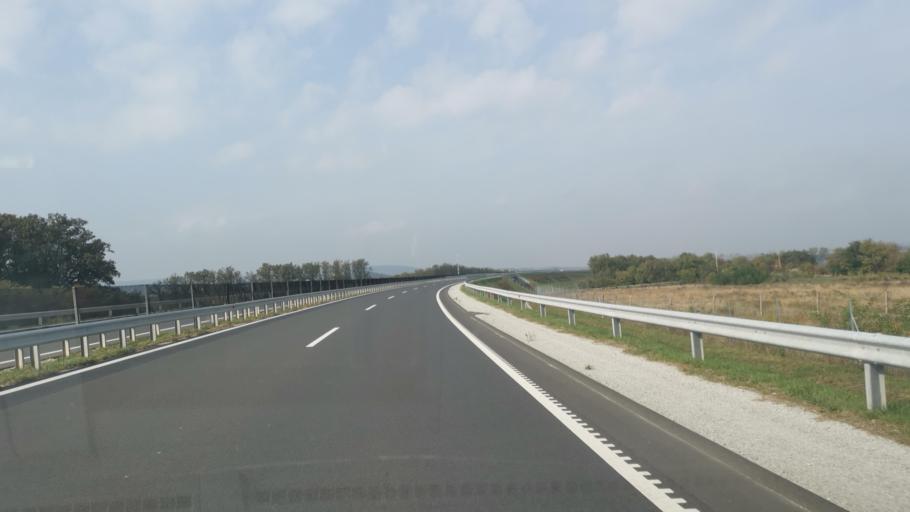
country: AT
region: Burgenland
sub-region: Politischer Bezirk Oberpullendorf
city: Deutschkreutz
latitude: 47.6307
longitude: 16.6329
